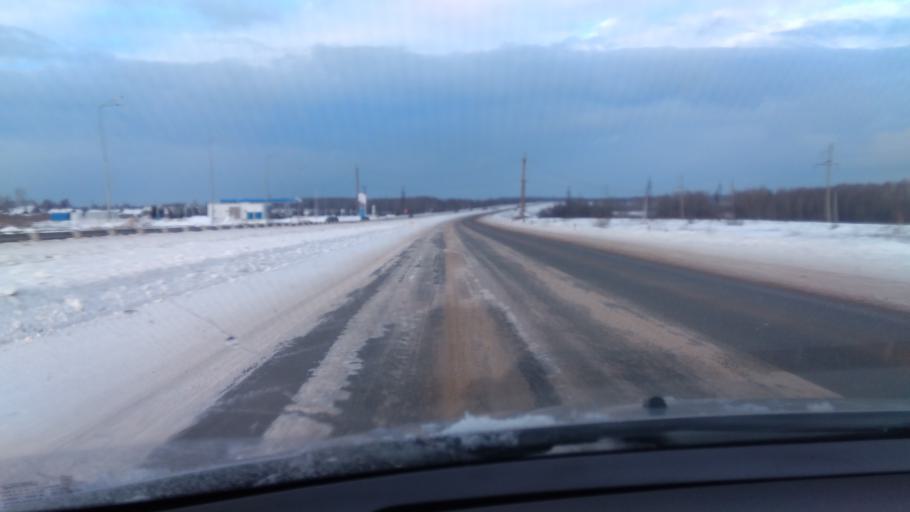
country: RU
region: Sverdlovsk
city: Tsementnyy
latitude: 57.4958
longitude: 60.1755
